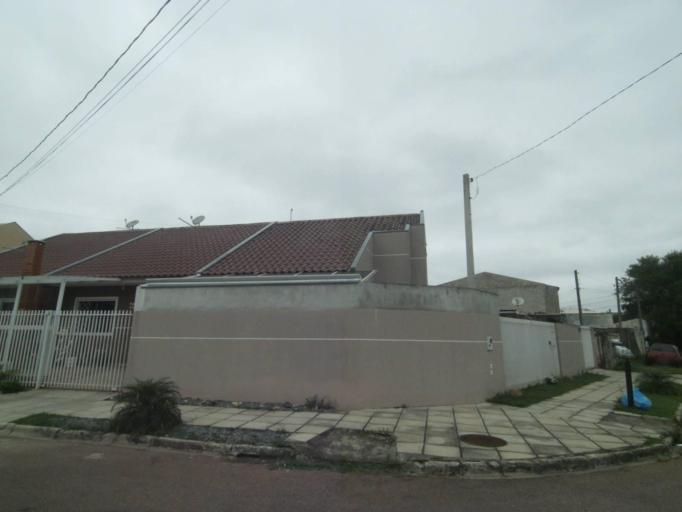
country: BR
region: Parana
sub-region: Araucaria
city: Araucaria
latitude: -25.5420
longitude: -49.3435
